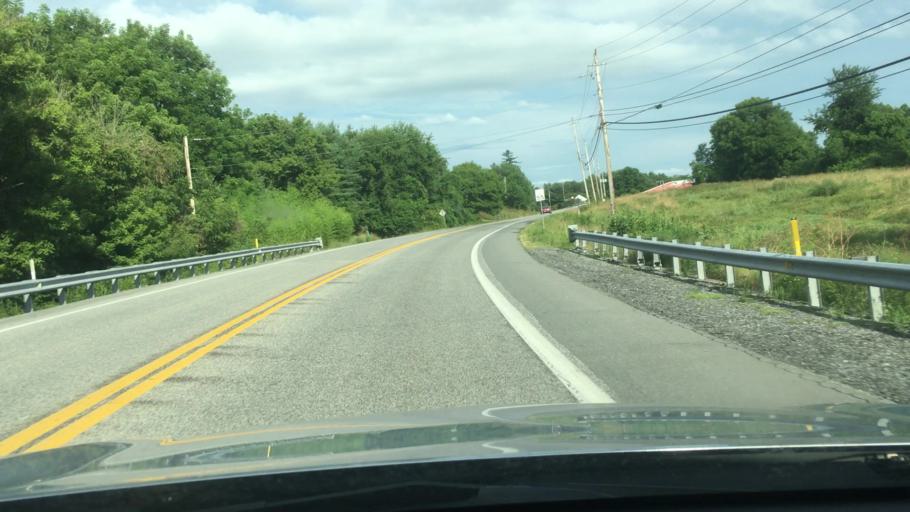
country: US
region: Pennsylvania
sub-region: York County
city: Dillsburg
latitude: 40.1008
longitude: -76.9808
